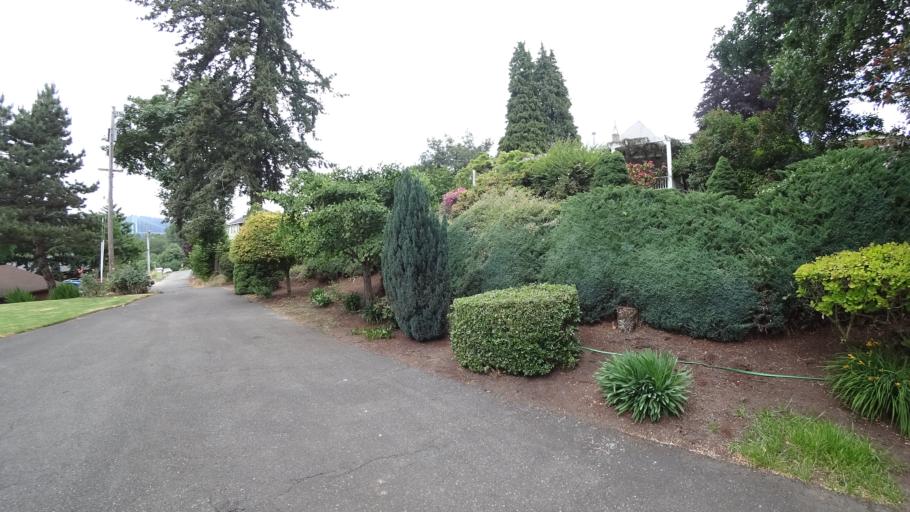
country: US
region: Oregon
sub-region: Washington County
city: West Haven
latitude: 45.5822
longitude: -122.7497
